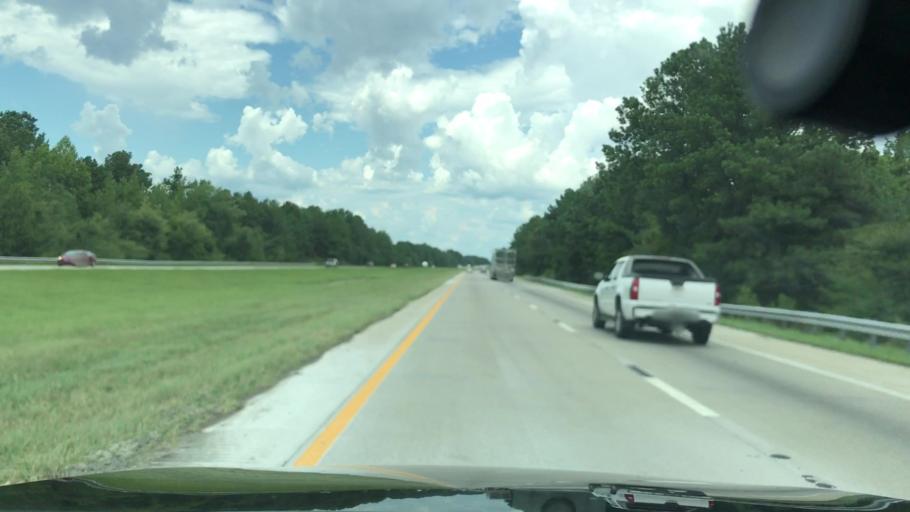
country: US
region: South Carolina
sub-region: Fairfield County
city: Winnsboro Mills
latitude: 34.3676
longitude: -80.9962
